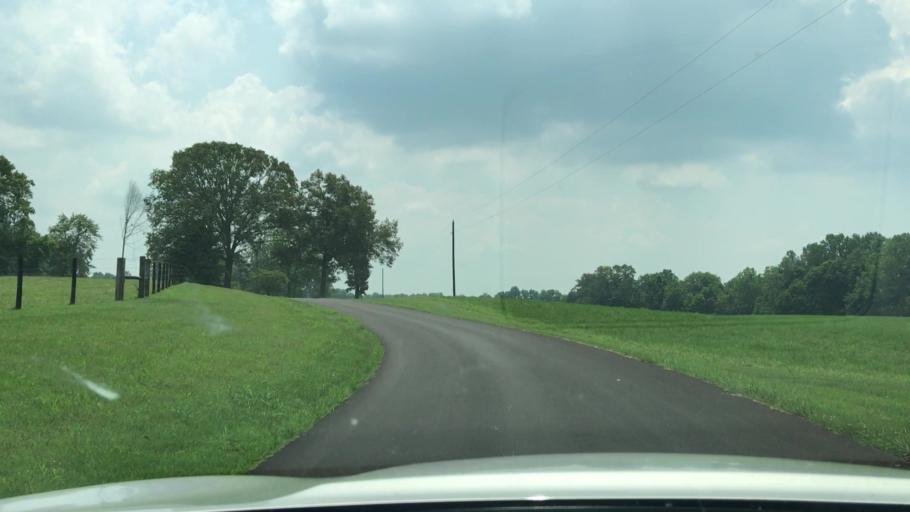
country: US
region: Kentucky
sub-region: Todd County
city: Elkton
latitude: 36.7714
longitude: -87.1415
